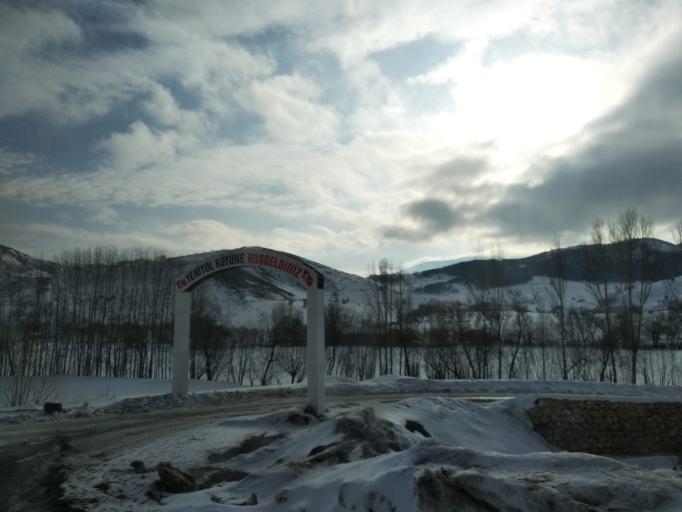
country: TR
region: Erzincan
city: Catalarmut
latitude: 39.9076
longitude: 39.4042
